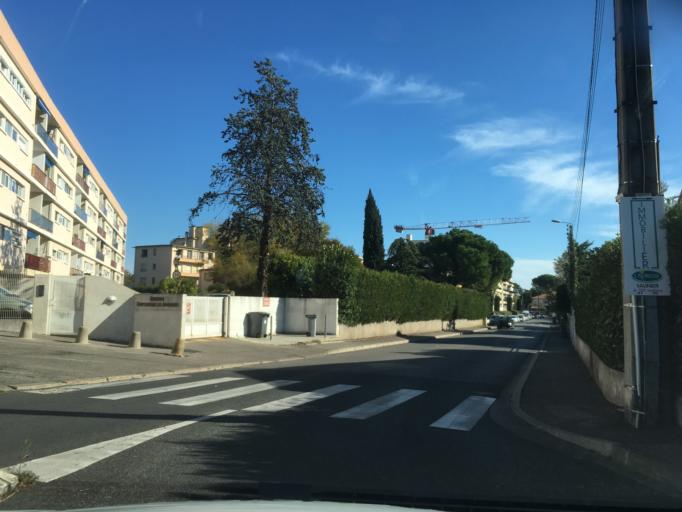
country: FR
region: Languedoc-Roussillon
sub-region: Departement de l'Herault
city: Montpellier
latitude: 43.6084
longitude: 3.8480
